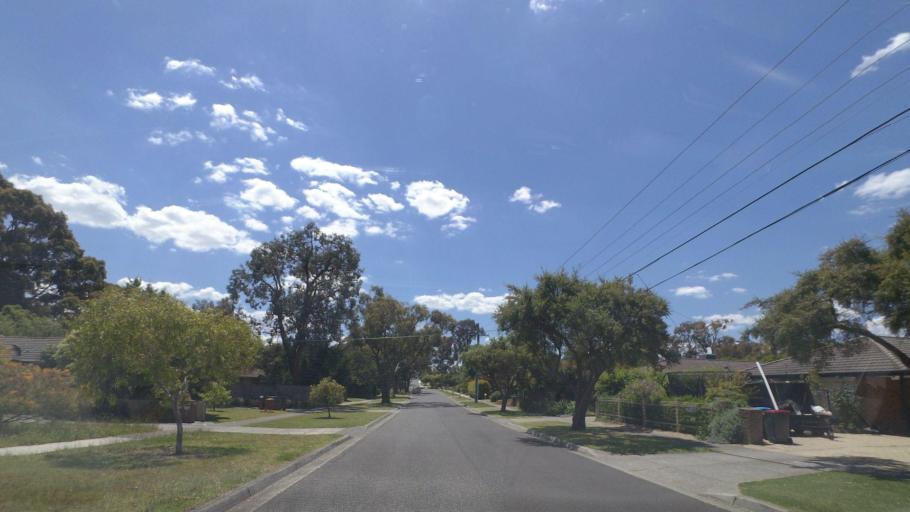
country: AU
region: Victoria
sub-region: Knox
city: Knoxfield
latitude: -37.8827
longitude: 145.2654
